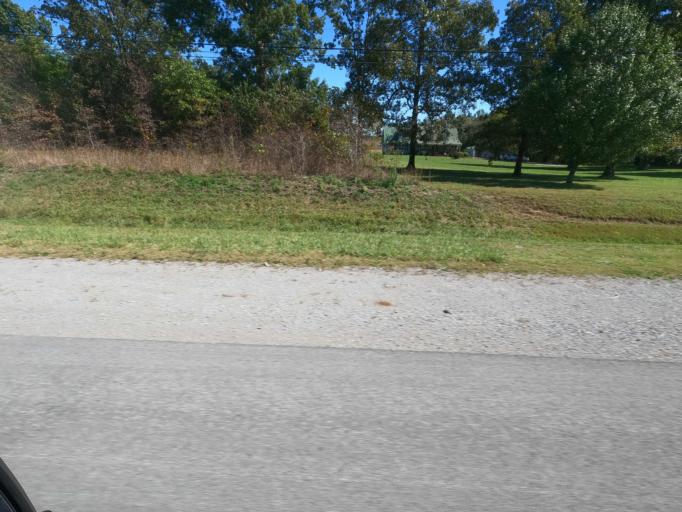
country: US
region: Tennessee
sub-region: Maury County
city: Mount Pleasant
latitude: 35.4307
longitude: -87.2810
